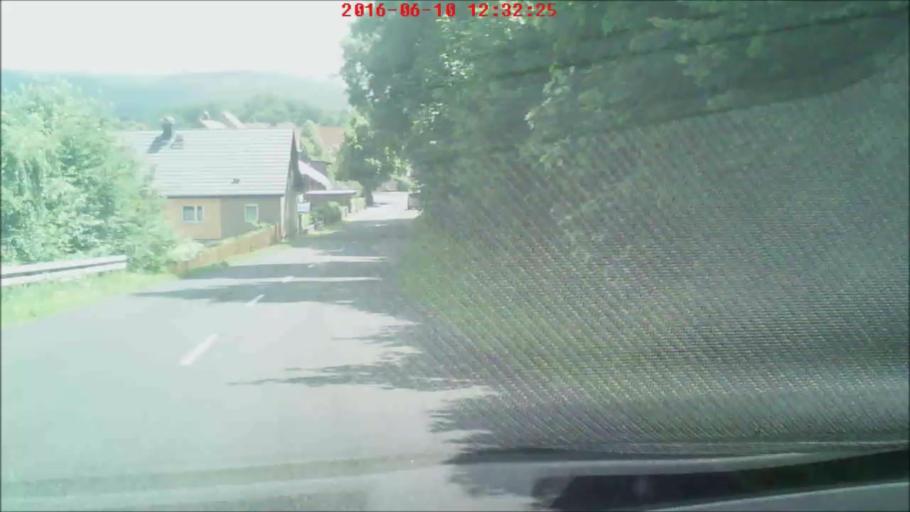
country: DE
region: Thuringia
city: Untermassfeld
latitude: 50.5299
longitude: 10.4110
